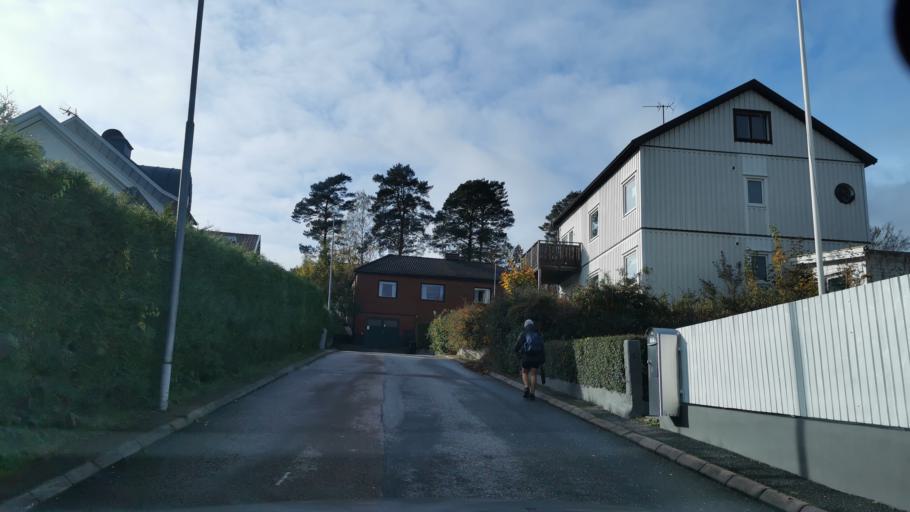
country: SE
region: Vaestra Goetaland
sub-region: Partille Kommun
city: Partille
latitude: 57.7261
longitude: 12.0742
